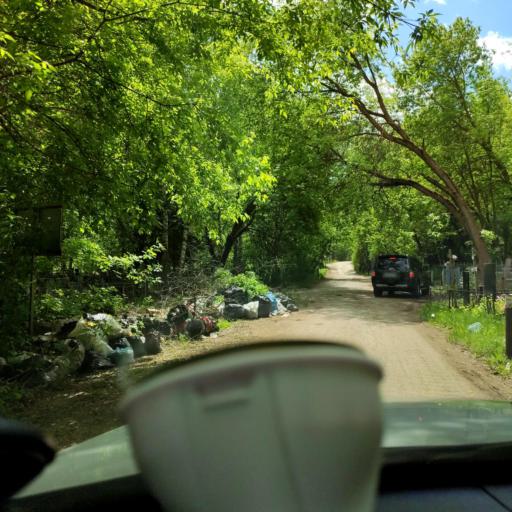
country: RU
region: Samara
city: Petra-Dubrava
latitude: 53.2762
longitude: 50.3231
